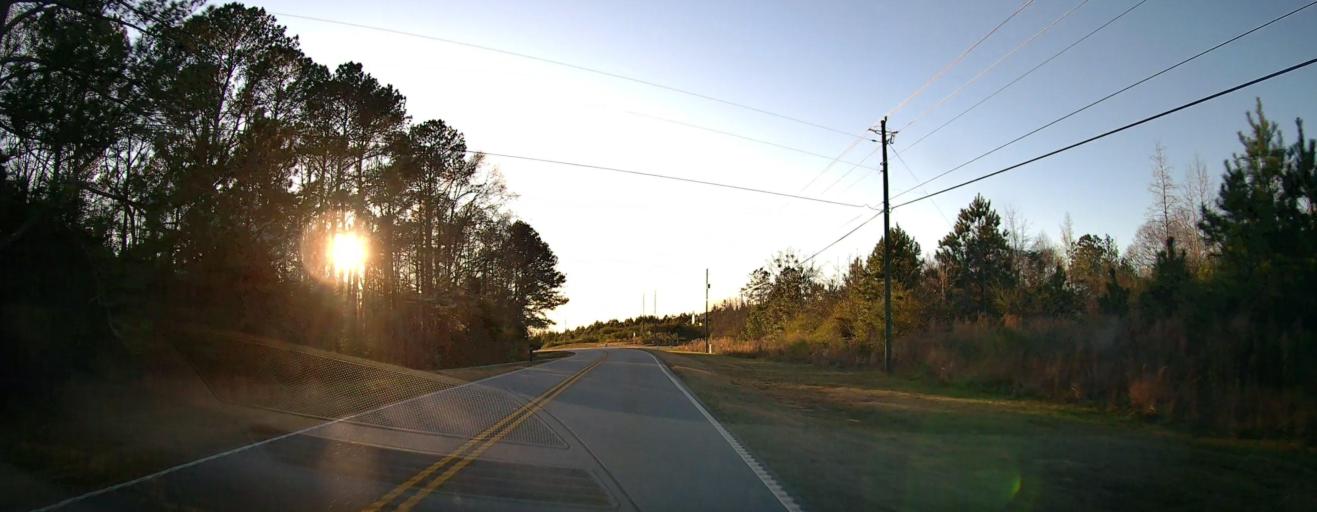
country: US
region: Georgia
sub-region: Harris County
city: Hamilton
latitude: 32.6732
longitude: -84.9384
